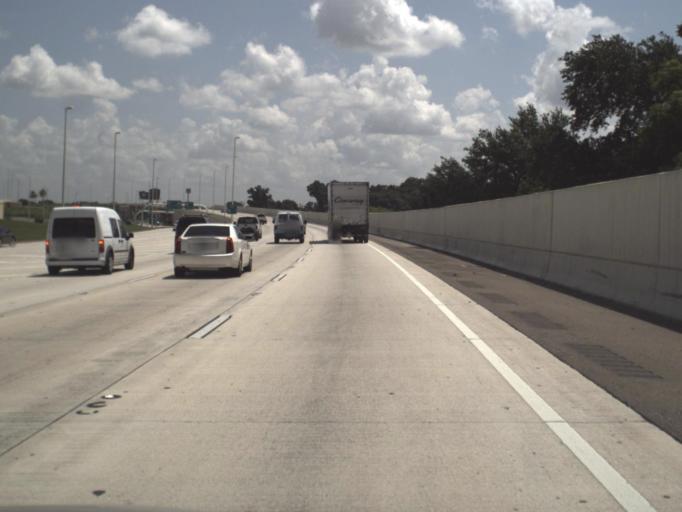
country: US
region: Florida
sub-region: Hillsborough County
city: East Lake-Orient Park
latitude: 27.9646
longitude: -82.4105
